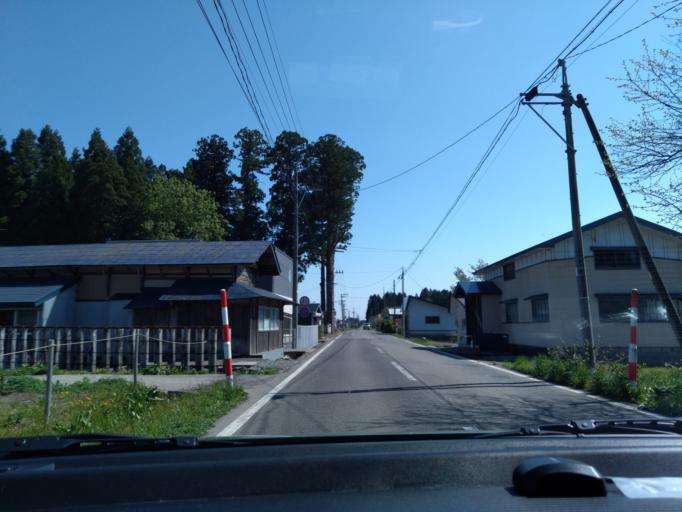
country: JP
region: Akita
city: Kakunodatemachi
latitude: 39.5511
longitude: 140.5860
